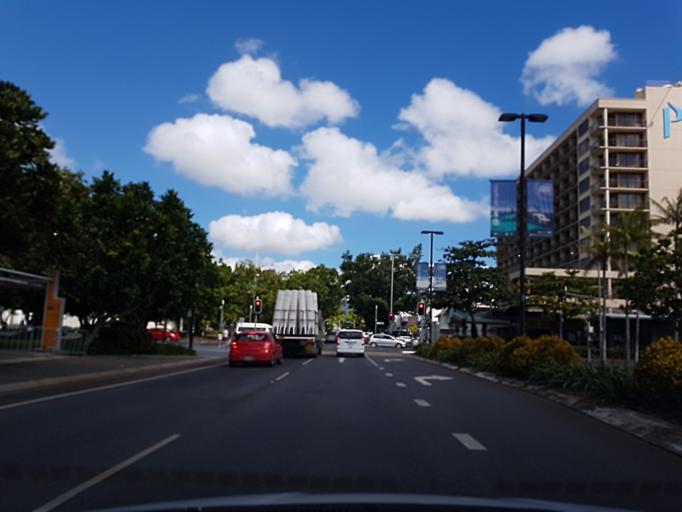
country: AU
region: Queensland
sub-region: Cairns
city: Cairns
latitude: -16.9218
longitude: 145.7797
